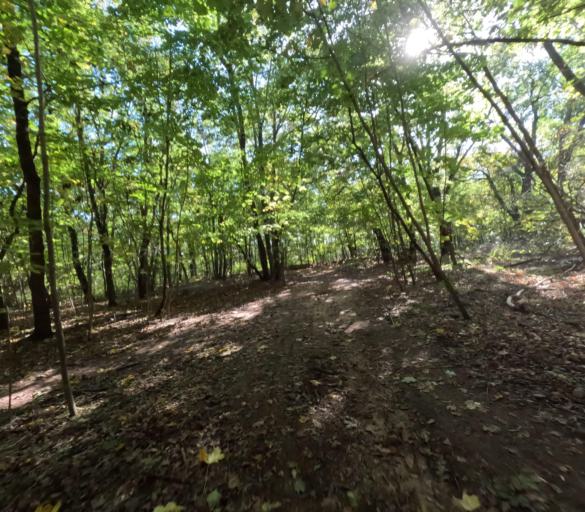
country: DE
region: Saxony
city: Albertstadt
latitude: 51.1059
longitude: 13.7429
